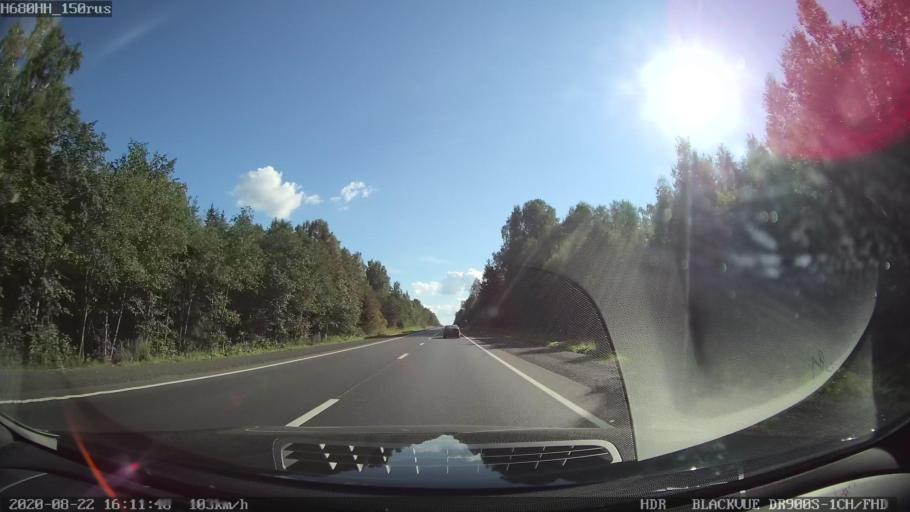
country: RU
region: Tverskaya
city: Rameshki
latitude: 57.4971
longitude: 36.2563
